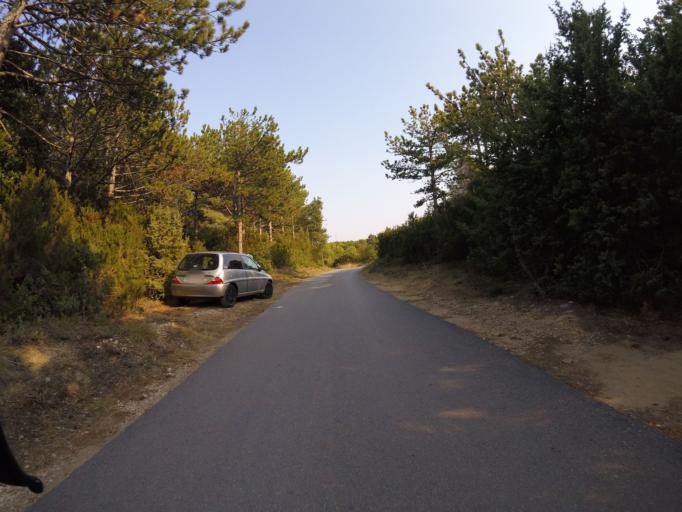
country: HR
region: Primorsko-Goranska
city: Lopar
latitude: 44.8438
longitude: 14.7268
